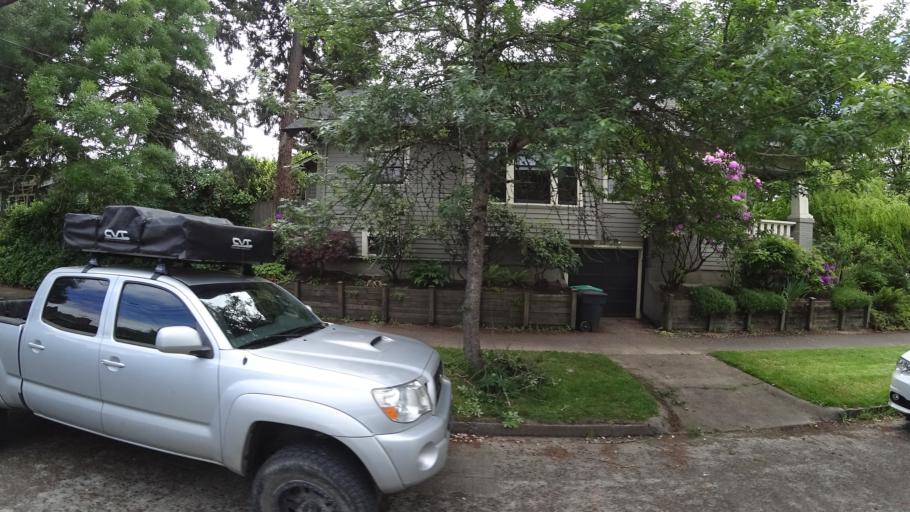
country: US
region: Oregon
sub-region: Multnomah County
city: Lents
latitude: 45.5079
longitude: -122.6061
